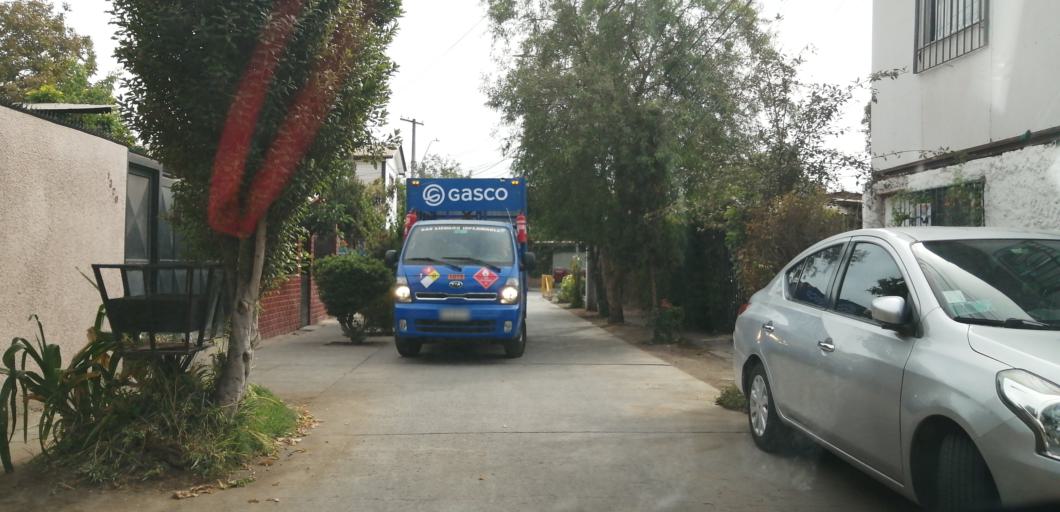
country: CL
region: Santiago Metropolitan
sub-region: Provincia de Santiago
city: Lo Prado
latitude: -33.4334
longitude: -70.7479
